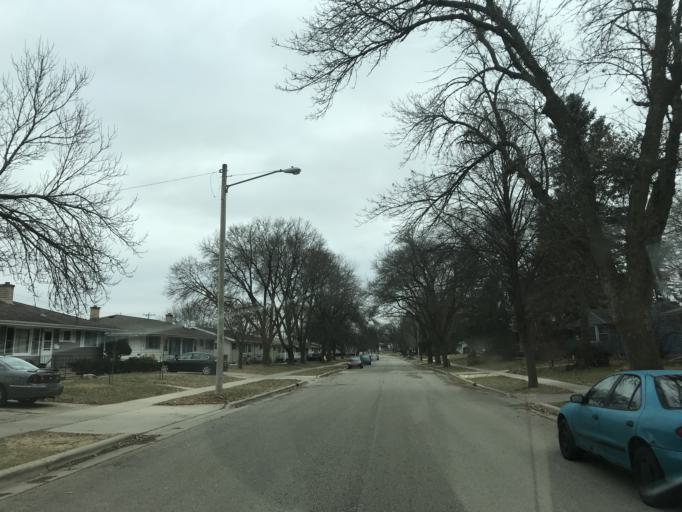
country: US
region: Wisconsin
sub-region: Dane County
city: Monona
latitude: 43.0658
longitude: -89.3120
